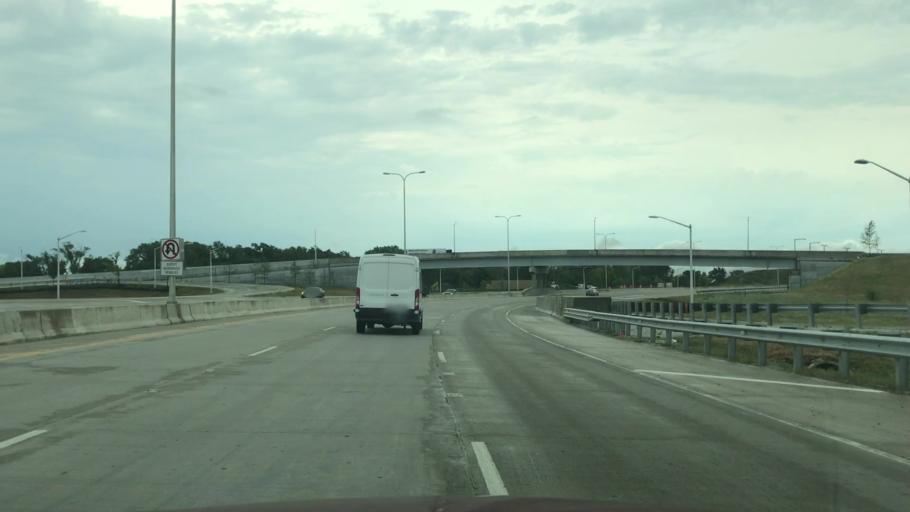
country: US
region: Illinois
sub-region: Cook County
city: Rosemont
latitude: 41.9903
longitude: -87.8810
